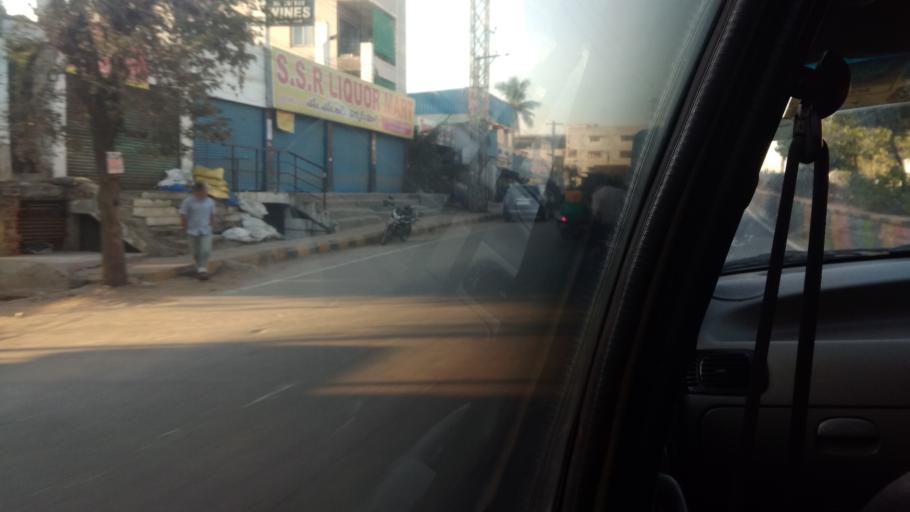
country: IN
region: Telangana
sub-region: Rangareddi
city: Uppal Kalan
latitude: 17.4274
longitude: 78.5506
